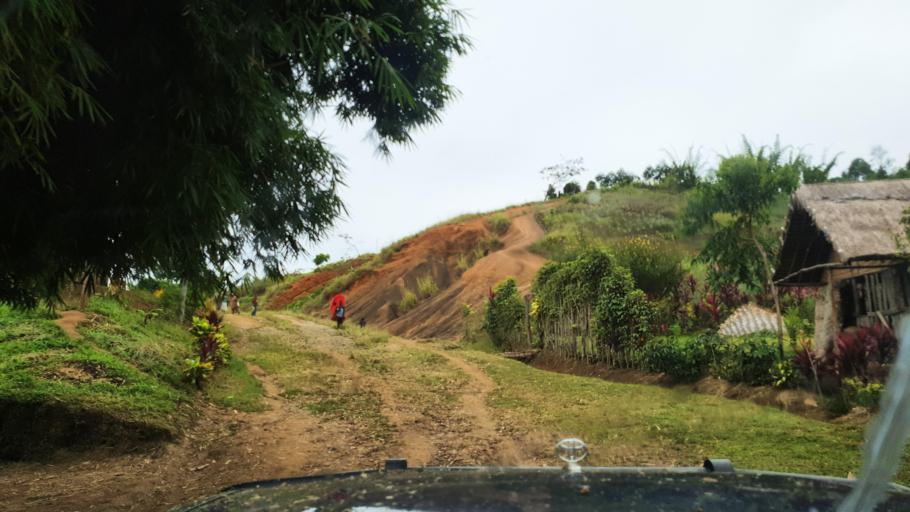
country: PG
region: Jiwaka
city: Minj
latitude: -5.9496
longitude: 144.7702
